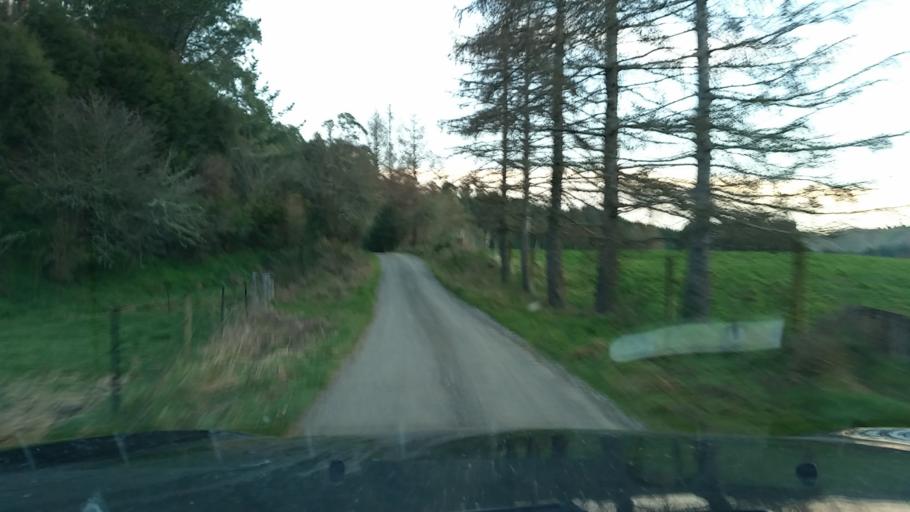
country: NZ
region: Marlborough
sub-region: Marlborough District
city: Blenheim
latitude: -41.4703
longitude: 173.7443
